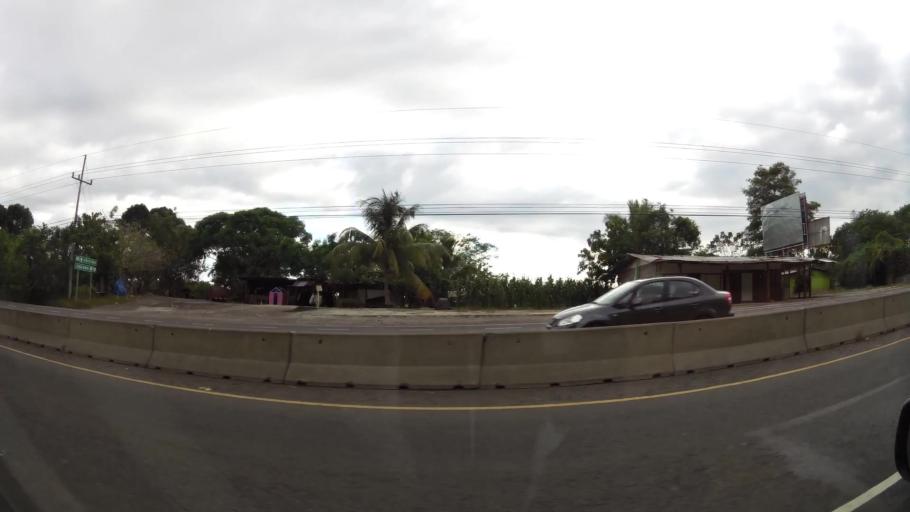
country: CR
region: Puntarenas
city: Esparza
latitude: 9.9144
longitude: -84.6796
